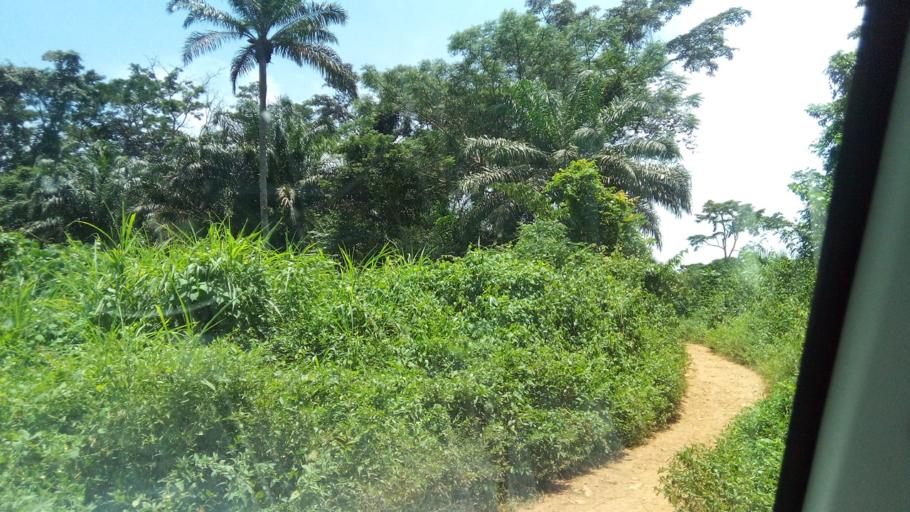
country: AO
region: Zaire
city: Mbanza Congo
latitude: -5.8095
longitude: 14.2447
